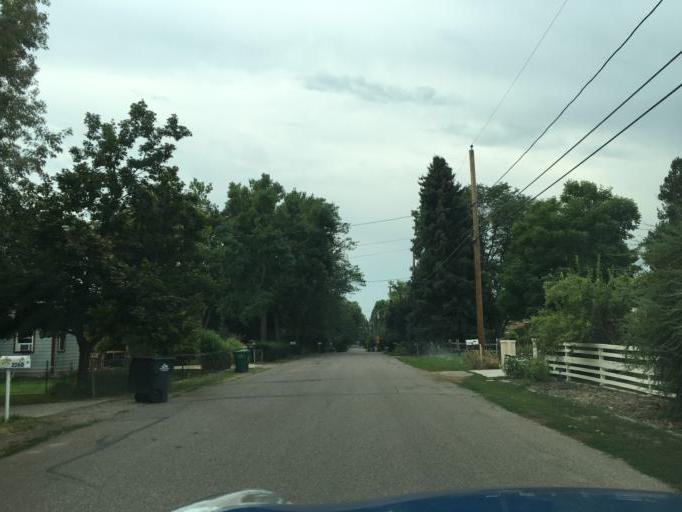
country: US
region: Colorado
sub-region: Jefferson County
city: Wheat Ridge
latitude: 39.7505
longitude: -105.1001
